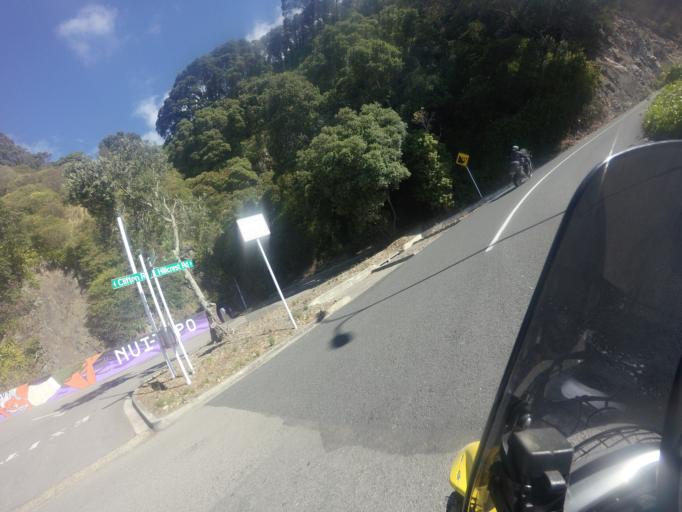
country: NZ
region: Bay of Plenty
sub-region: Whakatane District
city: Whakatane
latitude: -37.9514
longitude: 176.9991
